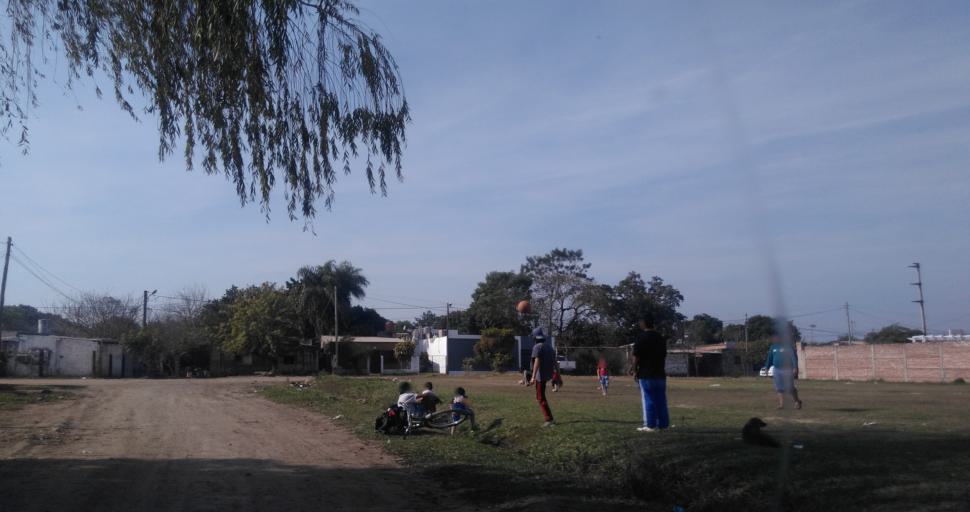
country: AR
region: Chaco
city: Fontana
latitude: -27.4282
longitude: -59.0165
